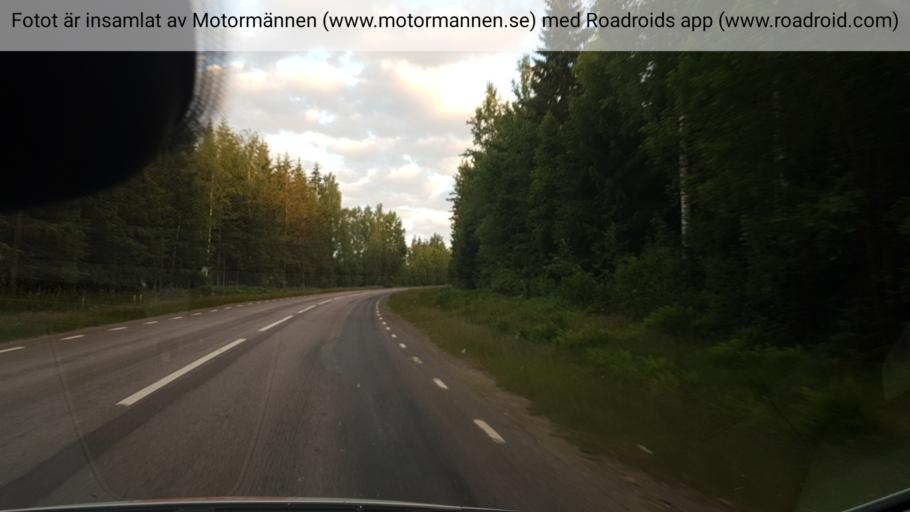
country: SE
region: Vaermland
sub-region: Sunne Kommun
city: Sunne
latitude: 59.7083
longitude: 13.1059
